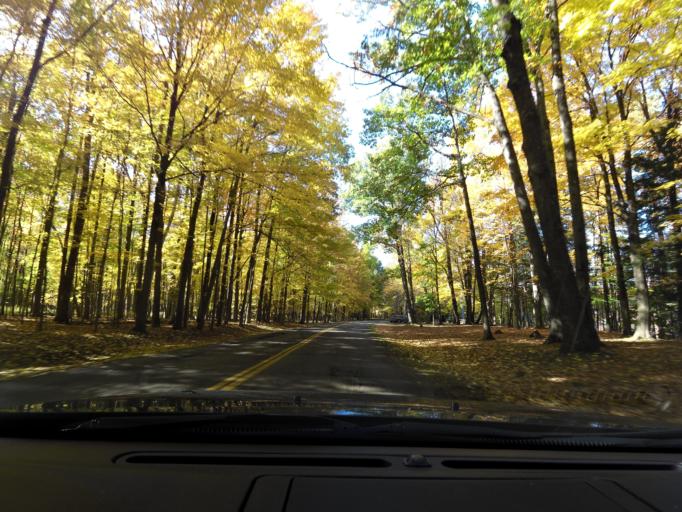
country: US
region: New York
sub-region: Wyoming County
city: Castile
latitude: 42.5947
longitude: -78.0191
